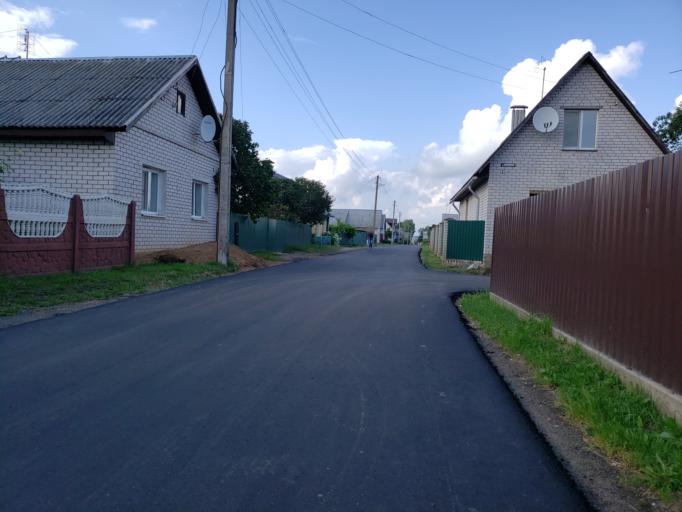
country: BY
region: Minsk
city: Chervyen'
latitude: 53.7077
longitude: 28.4214
